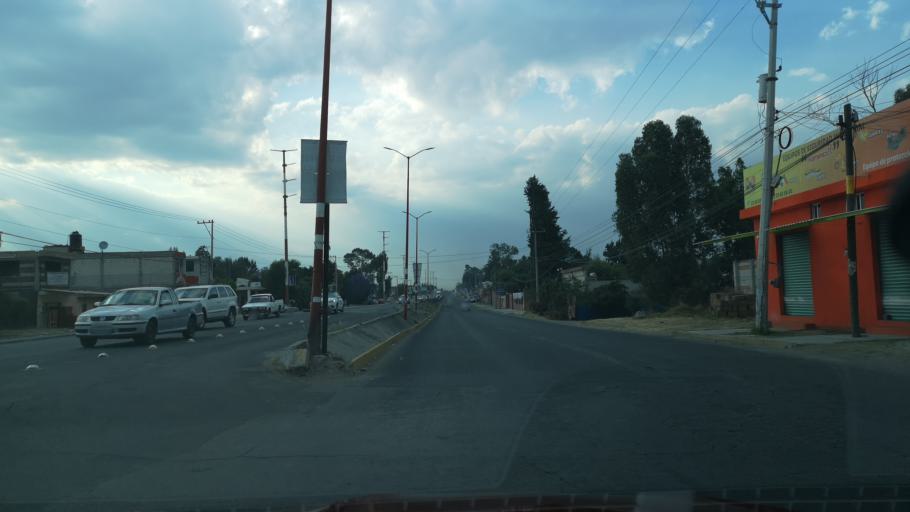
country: MX
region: Puebla
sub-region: Juan C. Bonilla
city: Santa Maria Zacatepec
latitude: 19.1071
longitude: -98.3510
